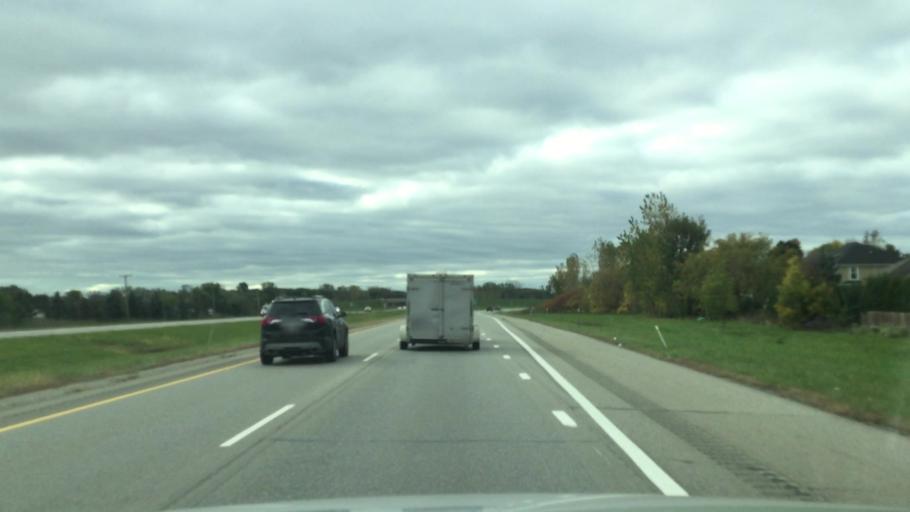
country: US
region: Michigan
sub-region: Macomb County
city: Shelby
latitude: 42.7202
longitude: -83.0266
